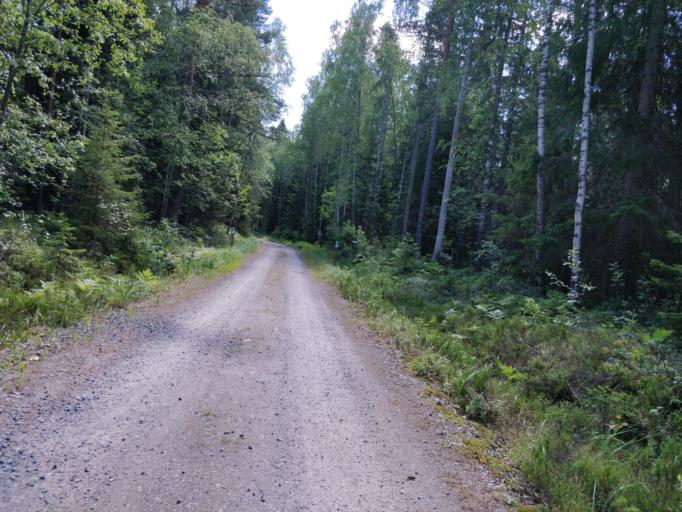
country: FI
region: Uusimaa
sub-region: Helsinki
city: Vihti
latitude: 60.3133
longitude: 24.4614
